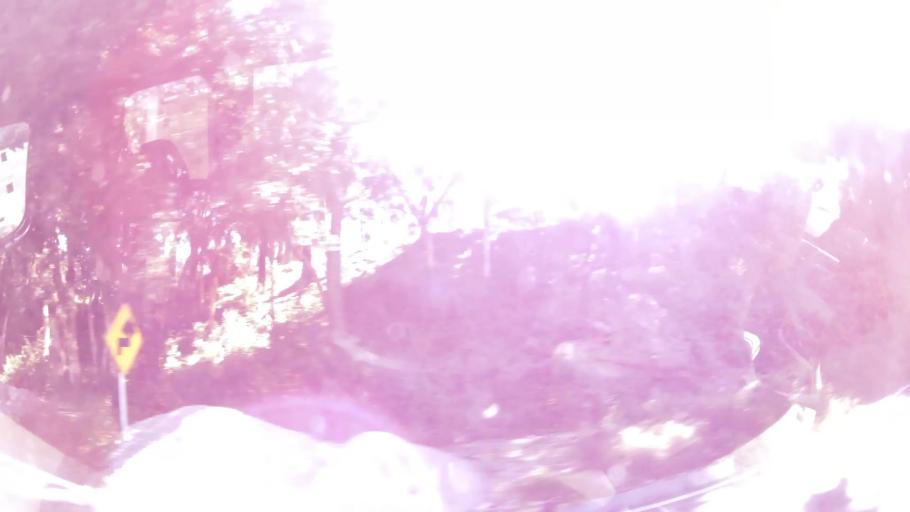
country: GT
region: Solola
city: Solola
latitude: 14.7645
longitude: -91.1780
